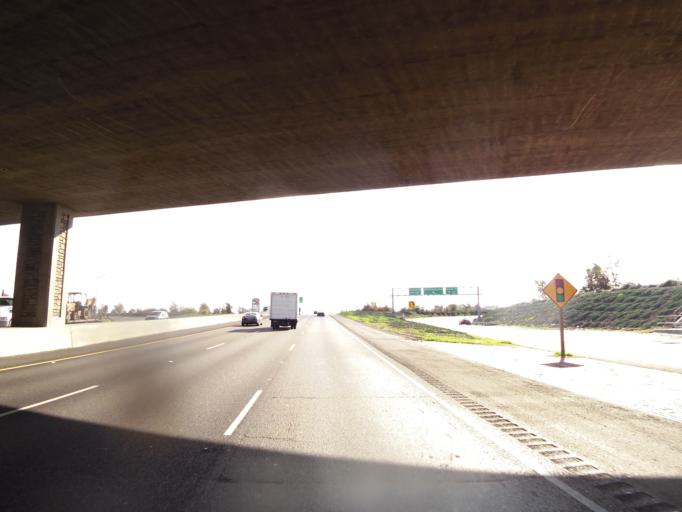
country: US
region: California
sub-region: Sacramento County
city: Laguna
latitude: 38.4378
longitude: -121.4019
